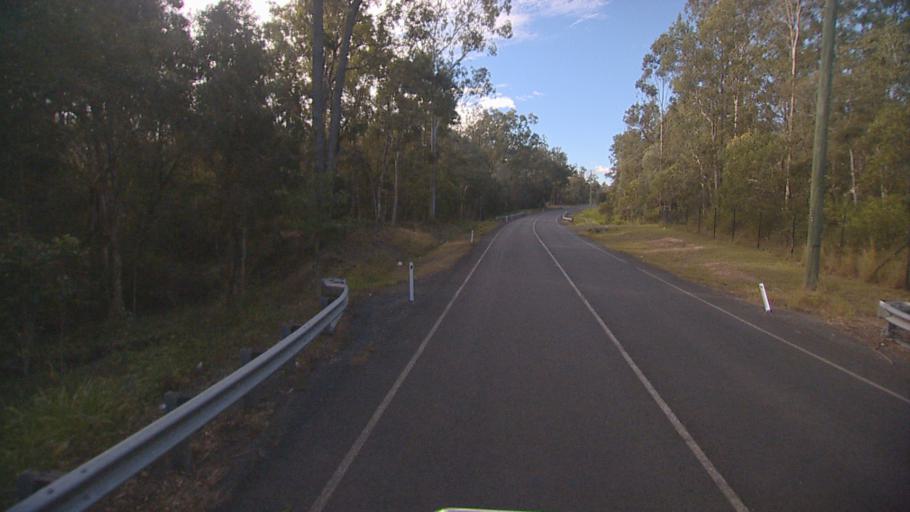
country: AU
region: Queensland
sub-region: Logan
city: North Maclean
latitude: -27.8099
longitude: 153.0579
